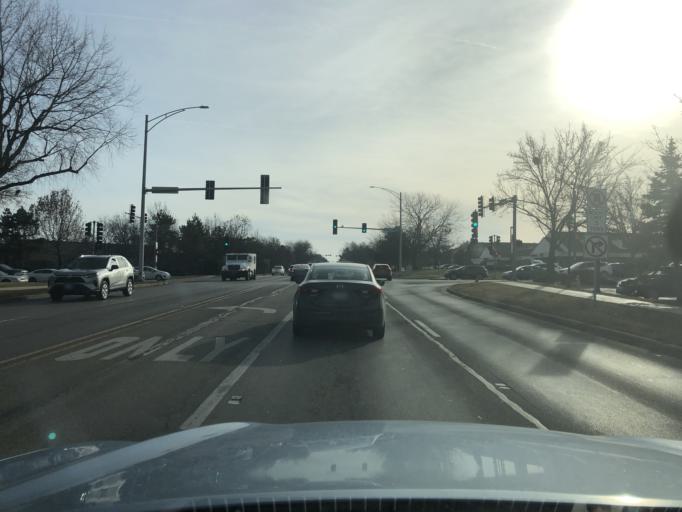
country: US
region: Illinois
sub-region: DuPage County
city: Bloomingdale
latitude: 41.9547
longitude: -88.0811
